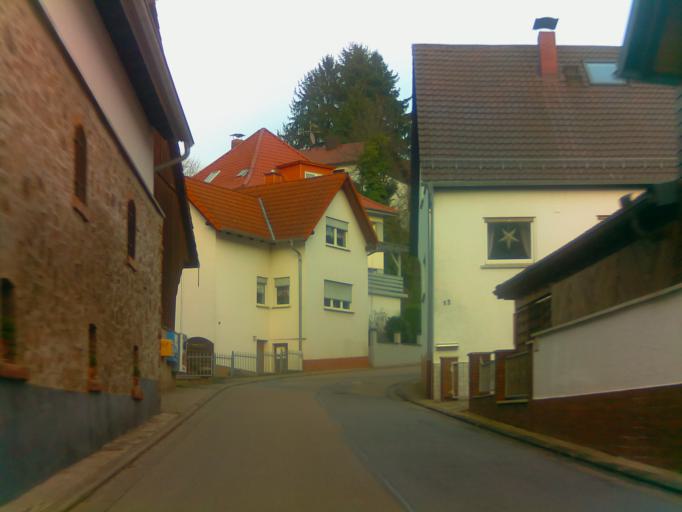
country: DE
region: Hesse
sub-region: Regierungsbezirk Darmstadt
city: Morlenbach
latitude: 49.5819
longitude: 8.7452
